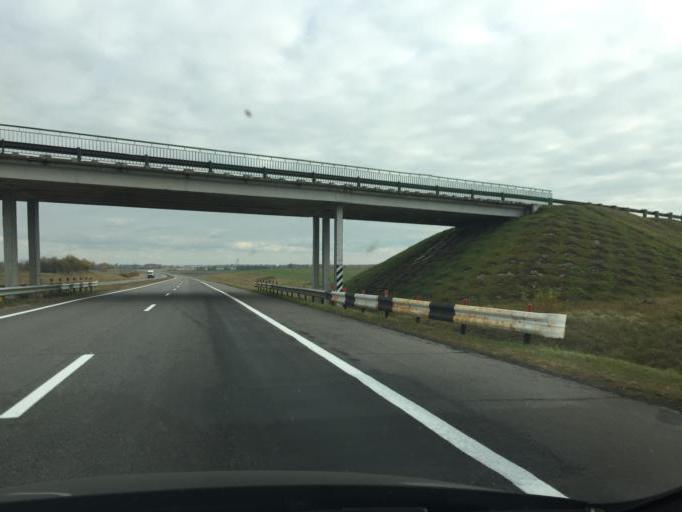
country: BY
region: Minsk
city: Stan'kava
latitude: 53.6767
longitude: 27.2082
